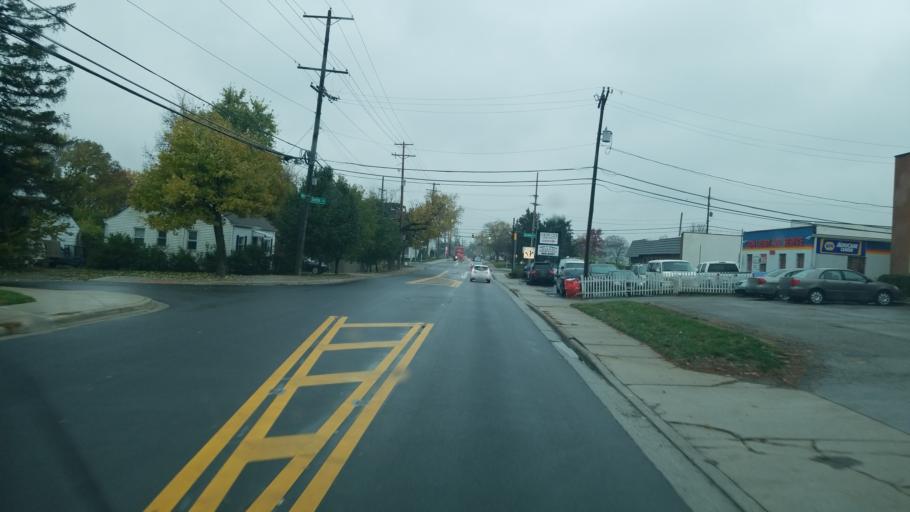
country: US
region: Ohio
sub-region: Franklin County
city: Grandview Heights
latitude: 39.9943
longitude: -83.0351
